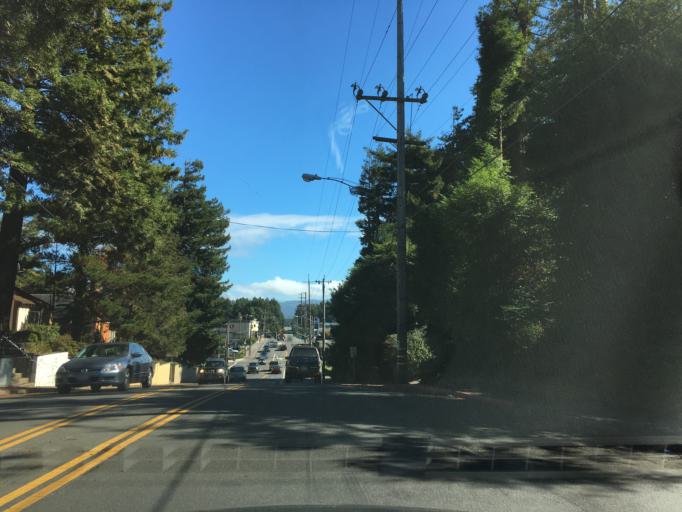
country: US
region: California
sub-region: Humboldt County
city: Cutten
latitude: 40.7804
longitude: -124.1411
